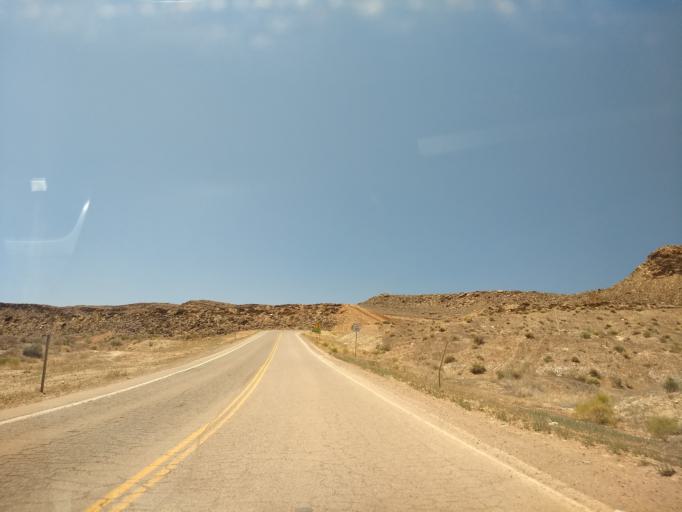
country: US
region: Utah
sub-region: Washington County
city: Washington
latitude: 37.1347
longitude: -113.4532
